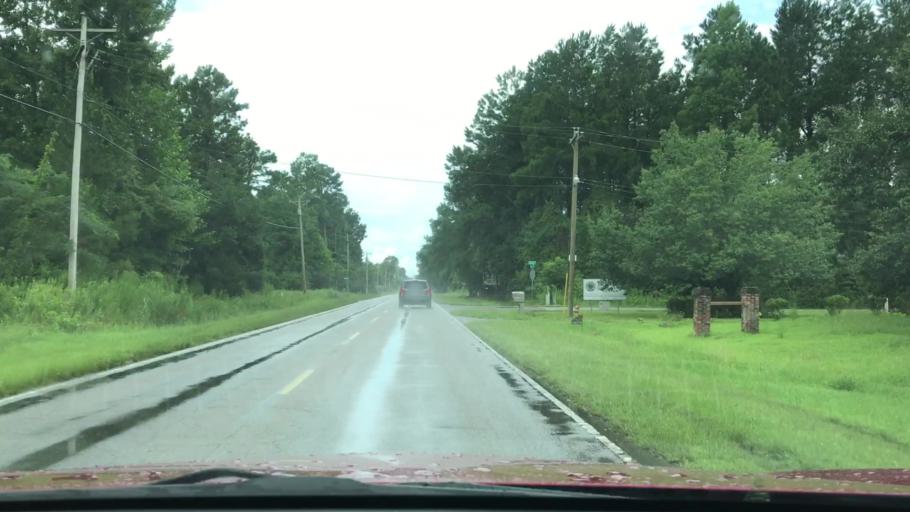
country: US
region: South Carolina
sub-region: Horry County
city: Red Hill
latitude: 33.8540
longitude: -79.0099
